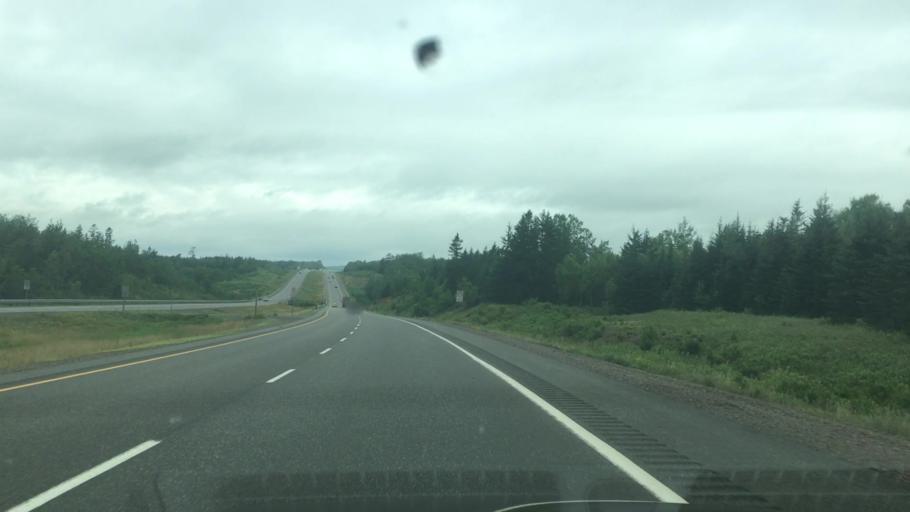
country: CA
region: Nova Scotia
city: Truro
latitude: 45.4439
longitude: -63.5916
